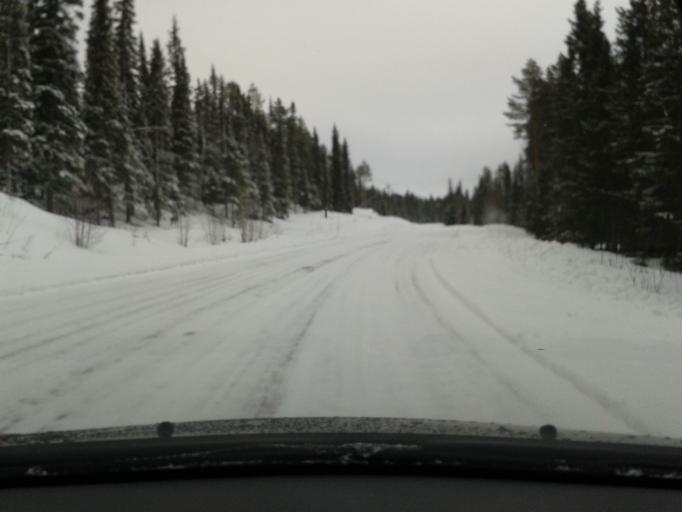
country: SE
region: Vaesterbotten
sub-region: Vilhelmina Kommun
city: Sjoberg
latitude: 65.2285
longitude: 15.9078
